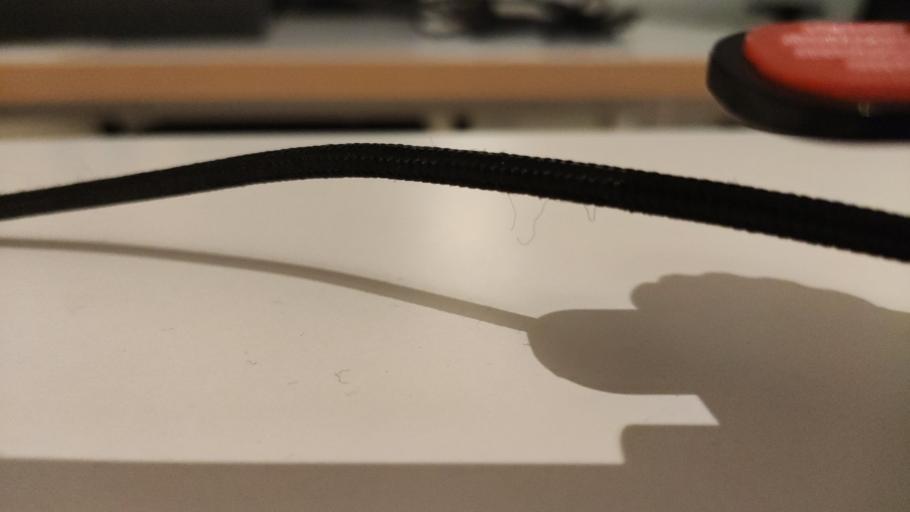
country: RU
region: Moskovskaya
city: Malaya Dubna
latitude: 55.8648
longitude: 38.9629
